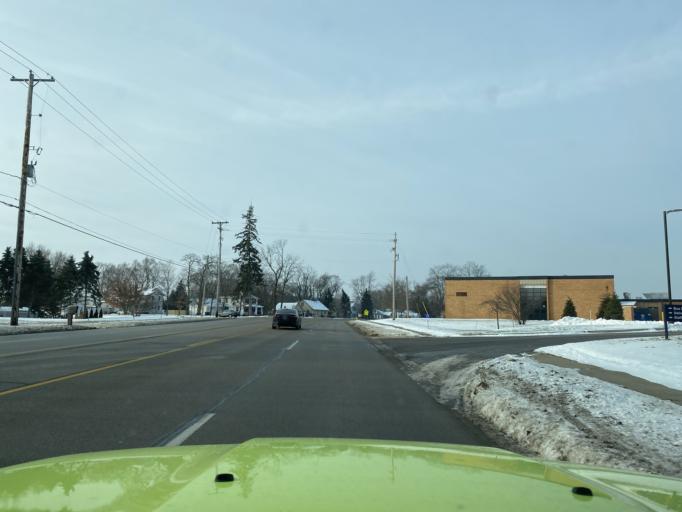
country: US
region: Michigan
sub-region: Ottawa County
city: Hudsonville
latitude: 42.8861
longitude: -85.8743
